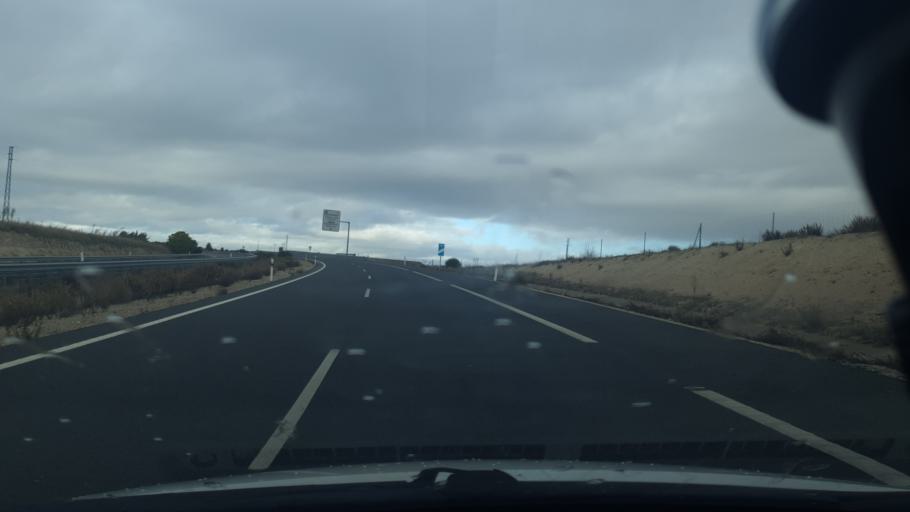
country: ES
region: Castille and Leon
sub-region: Provincia de Segovia
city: Cuellar
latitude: 41.4018
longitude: -4.2929
